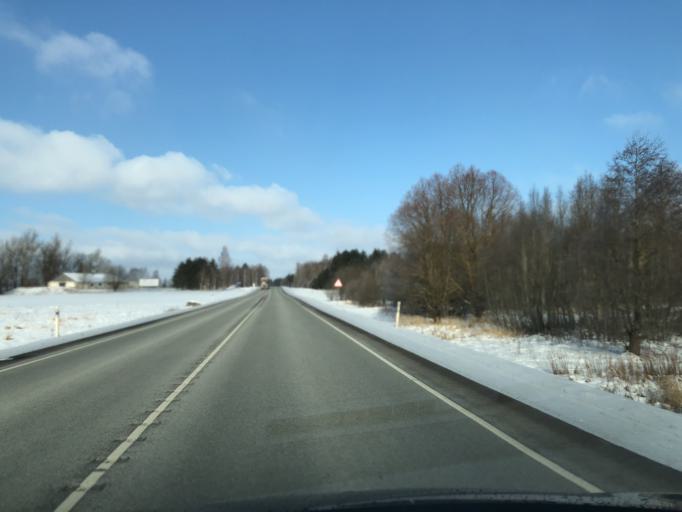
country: EE
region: Jaervamaa
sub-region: Paide linn
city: Paide
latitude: 58.8324
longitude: 25.7425
